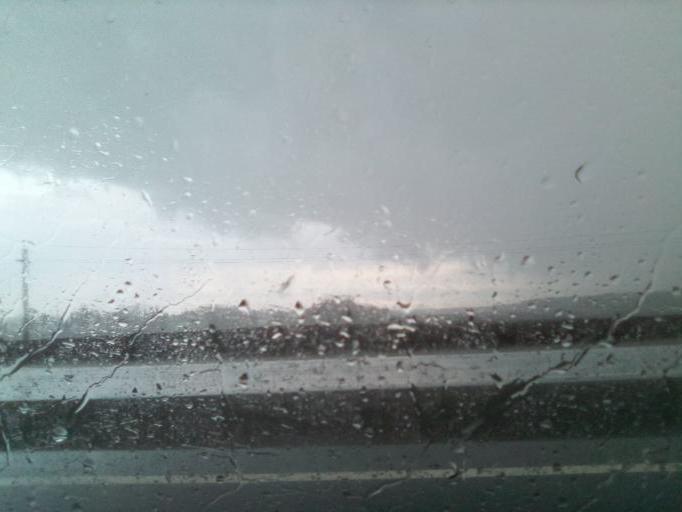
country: RU
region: Chelyabinsk
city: Poletayevo
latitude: 54.9873
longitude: 61.0381
